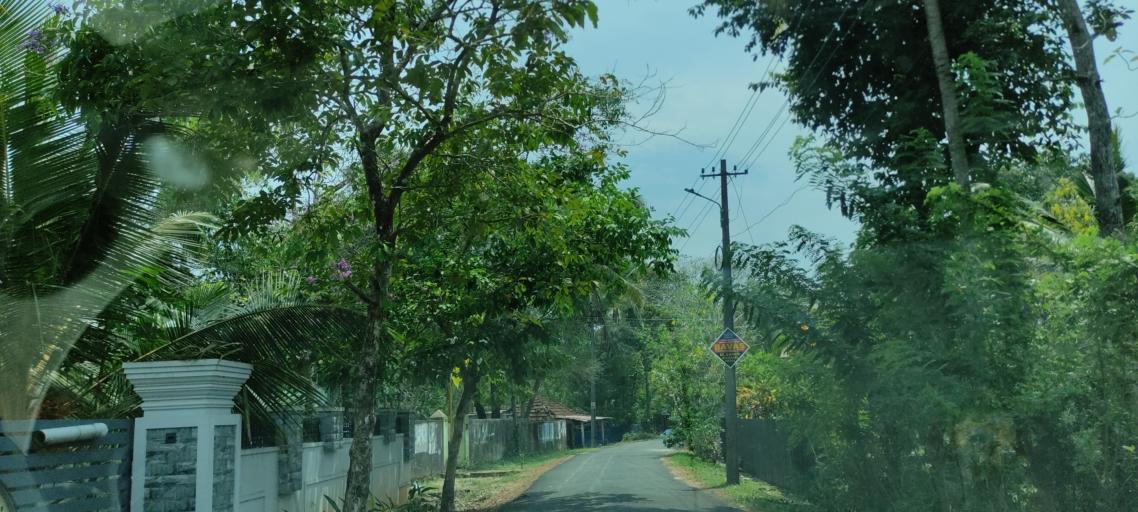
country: IN
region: Kerala
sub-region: Alappuzha
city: Vayalar
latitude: 9.7135
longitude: 76.3402
